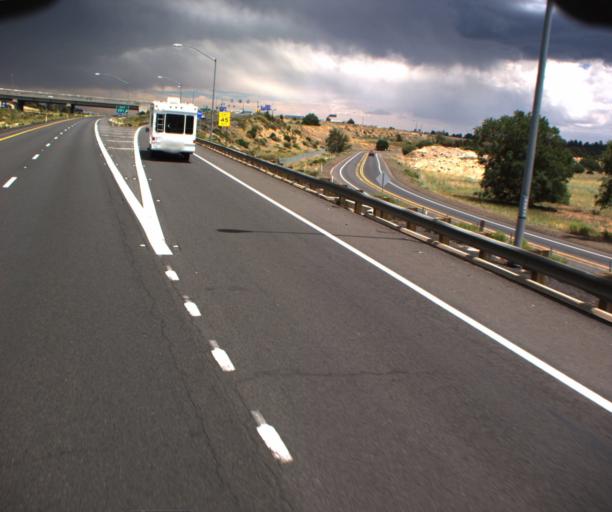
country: US
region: Arizona
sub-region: Coconino County
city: Flagstaff
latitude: 35.2152
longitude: -111.5861
